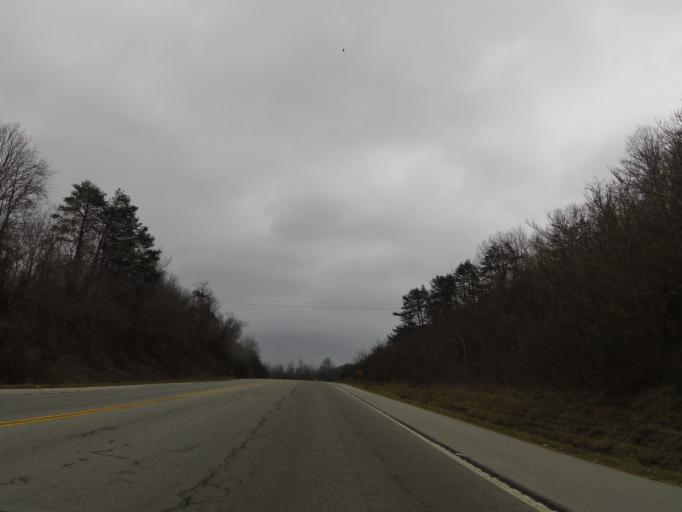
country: US
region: Tennessee
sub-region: Scott County
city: Huntsville
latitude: 36.3644
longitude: -84.5793
